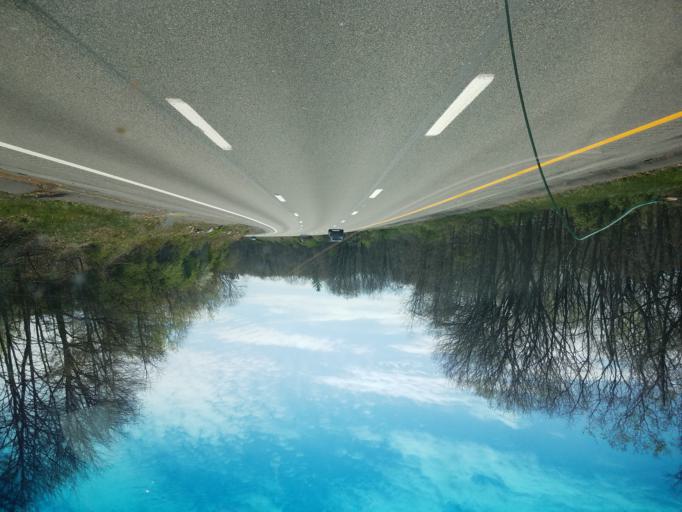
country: US
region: West Virginia
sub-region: Raleigh County
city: Shady Spring
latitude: 37.6595
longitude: -81.1139
